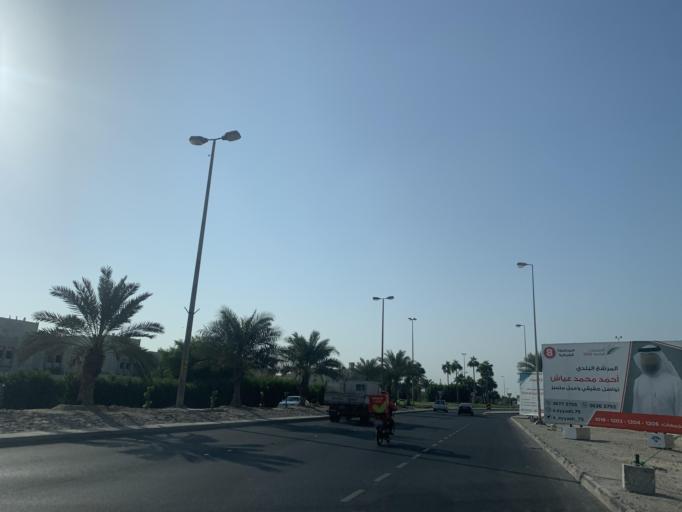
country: BH
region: Central Governorate
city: Madinat Hamad
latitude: 26.1413
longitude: 50.4993
